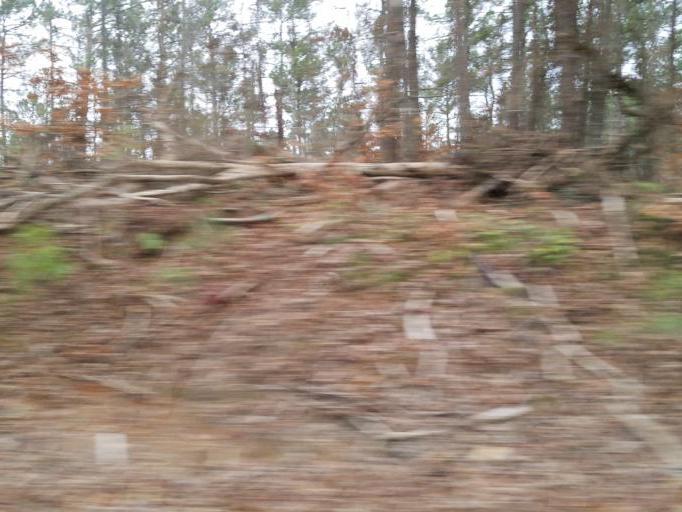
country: US
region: Georgia
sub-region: Dawson County
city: Dawsonville
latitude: 34.4454
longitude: -84.1054
